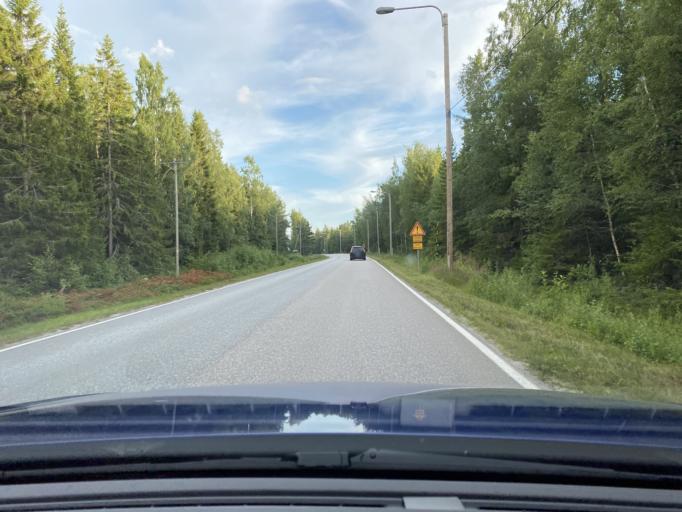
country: FI
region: Ostrobothnia
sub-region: Vaasa
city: Korsnaes
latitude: 62.9472
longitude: 21.1757
